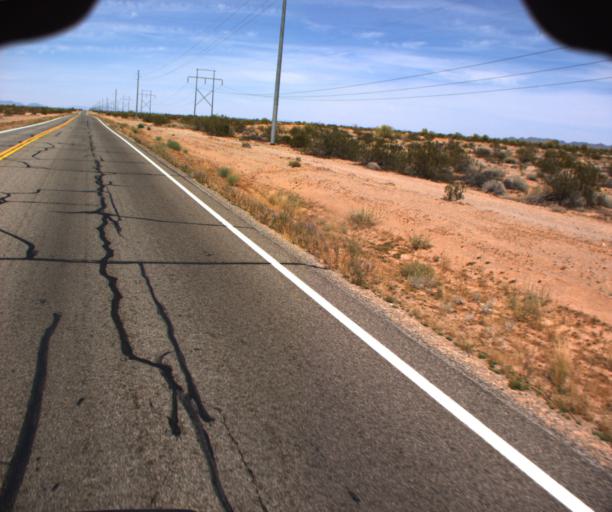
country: US
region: Arizona
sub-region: La Paz County
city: Quartzsite
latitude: 33.7880
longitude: -114.2170
